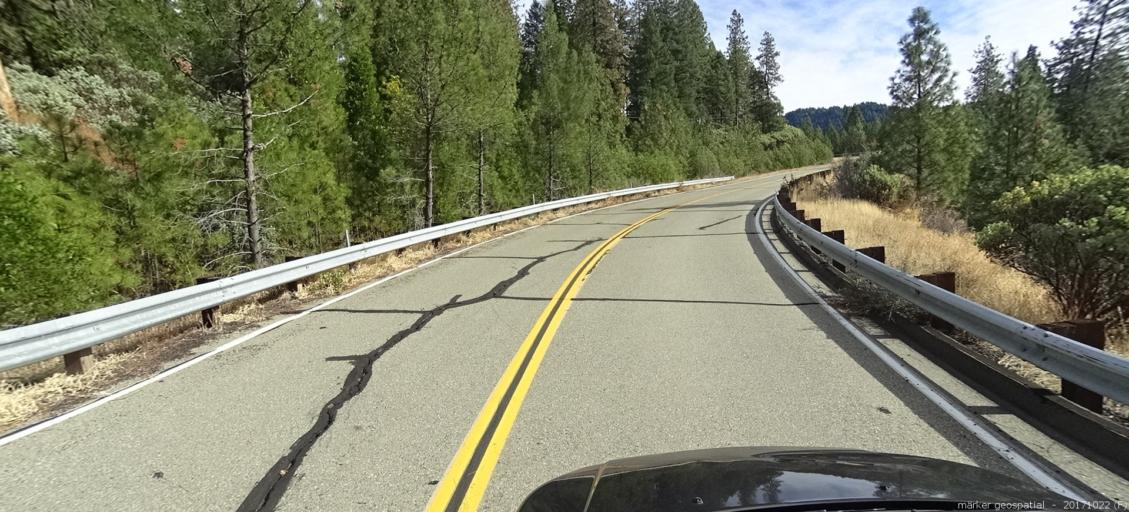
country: US
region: California
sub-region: Siskiyou County
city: Dunsmuir
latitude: 41.0625
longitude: -122.3725
